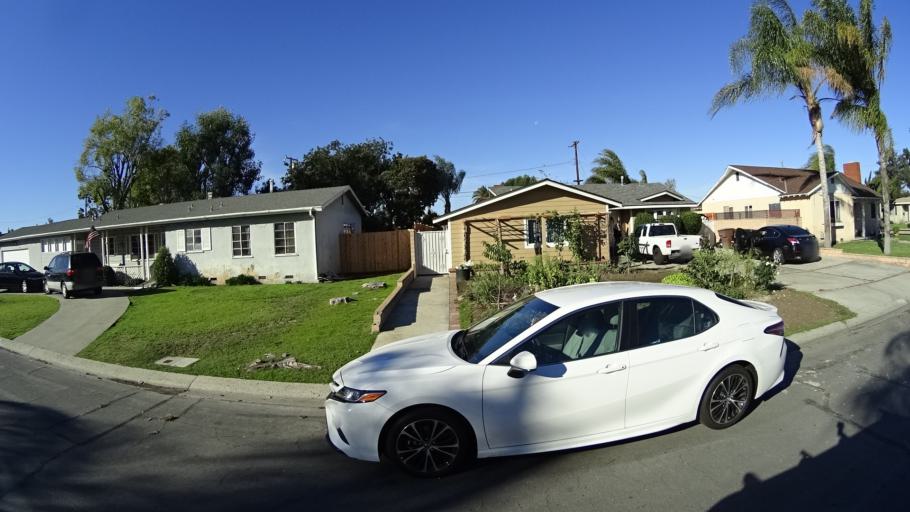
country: US
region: California
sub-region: Orange County
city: Garden Grove
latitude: 33.7695
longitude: -117.9687
